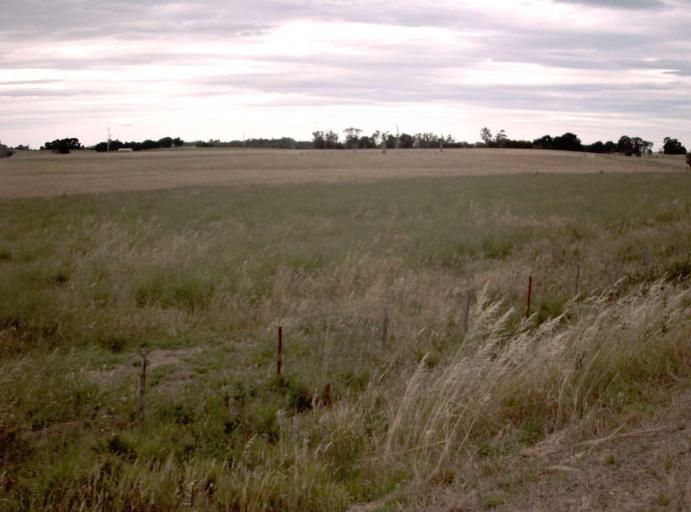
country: AU
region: Victoria
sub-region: East Gippsland
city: Bairnsdale
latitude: -37.9771
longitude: 147.4497
